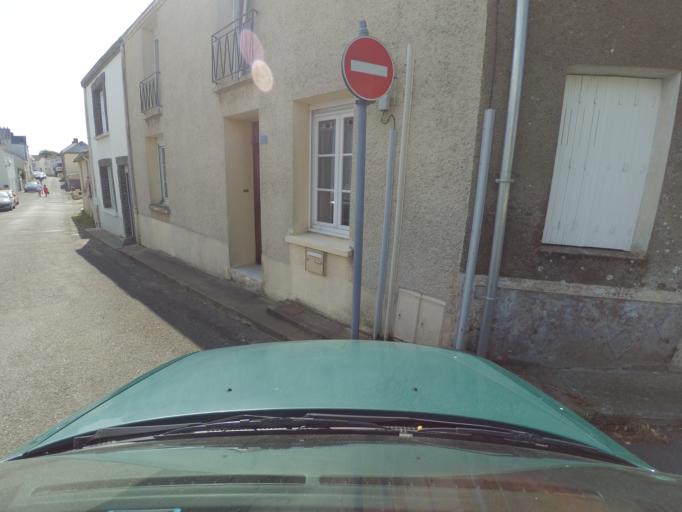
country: FR
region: Pays de la Loire
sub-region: Departement de la Vendee
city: Rocheserviere
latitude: 46.9390
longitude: -1.5116
